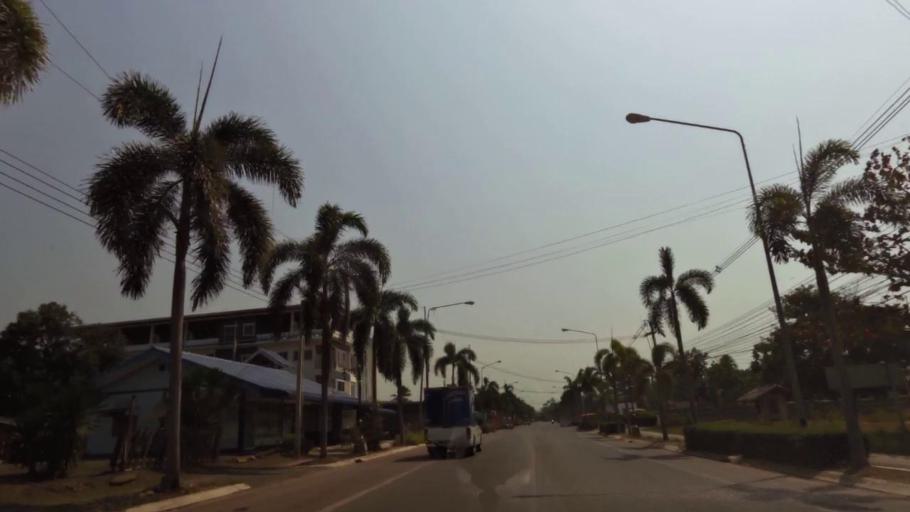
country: TH
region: Chanthaburi
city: Tha Mai
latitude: 12.5544
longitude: 101.9209
